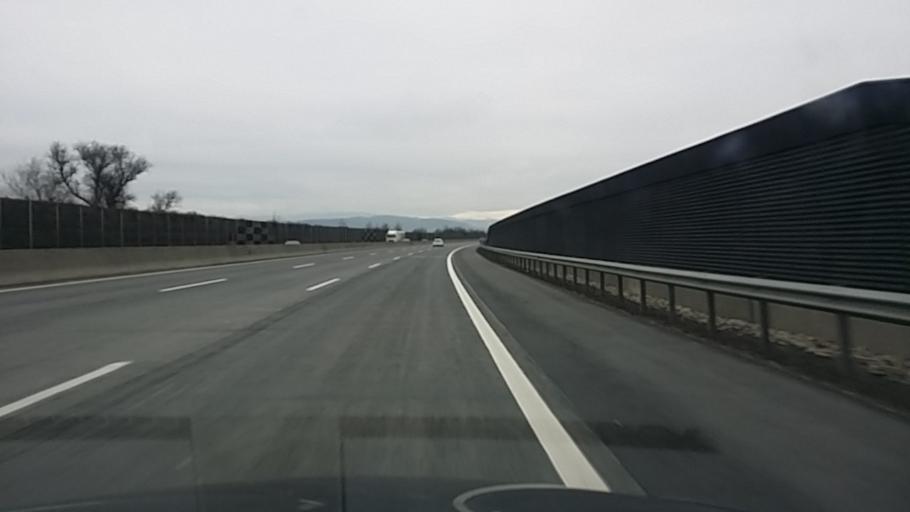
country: AT
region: Lower Austria
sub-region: Politischer Bezirk Melk
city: Erlauf
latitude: 48.1869
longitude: 15.1928
